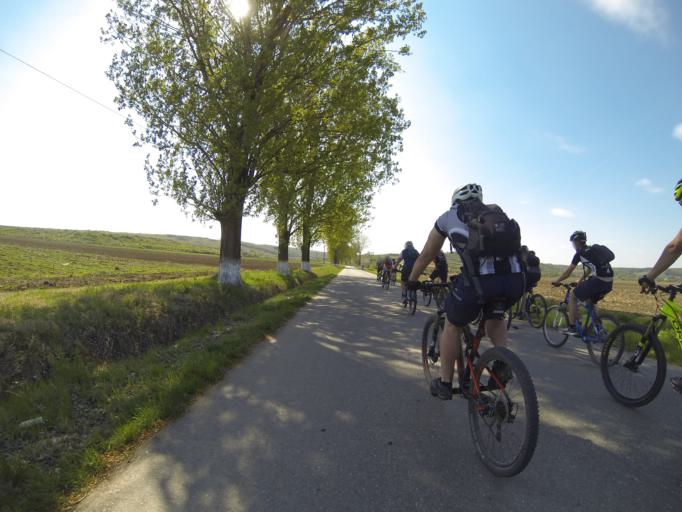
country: RO
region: Gorj
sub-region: Comuna Crusetu
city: Crusetu
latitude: 44.6205
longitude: 23.6775
